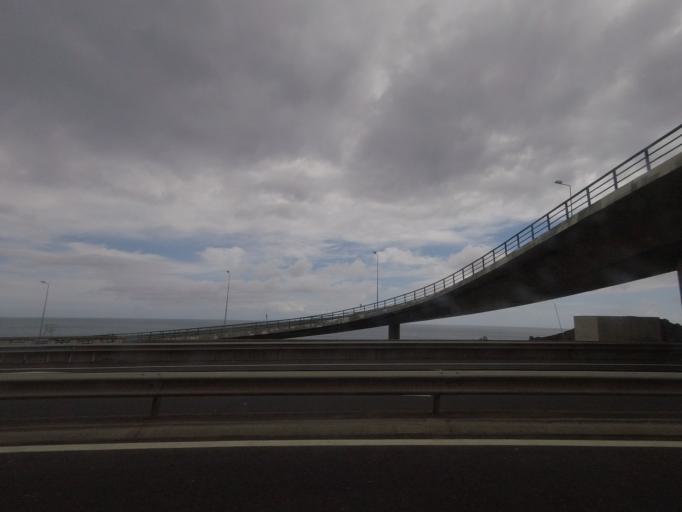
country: PT
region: Madeira
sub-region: Santa Cruz
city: Santa Cruz
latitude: 32.6808
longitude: -16.7978
